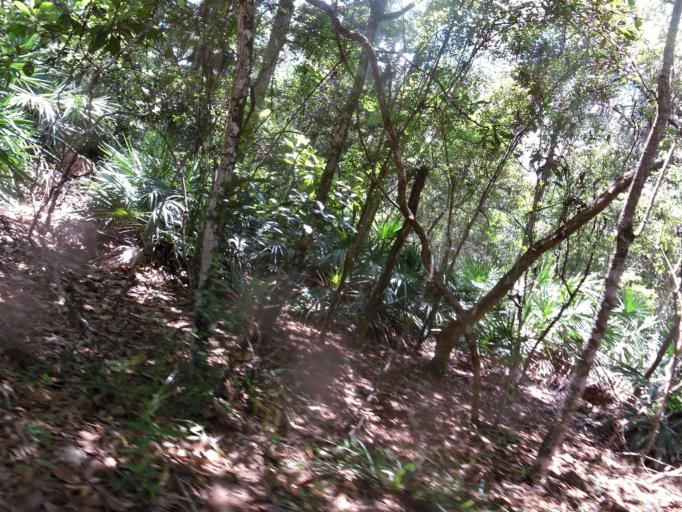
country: US
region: Florida
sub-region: Flagler County
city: Flagler Beach
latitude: 29.4130
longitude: -81.1300
